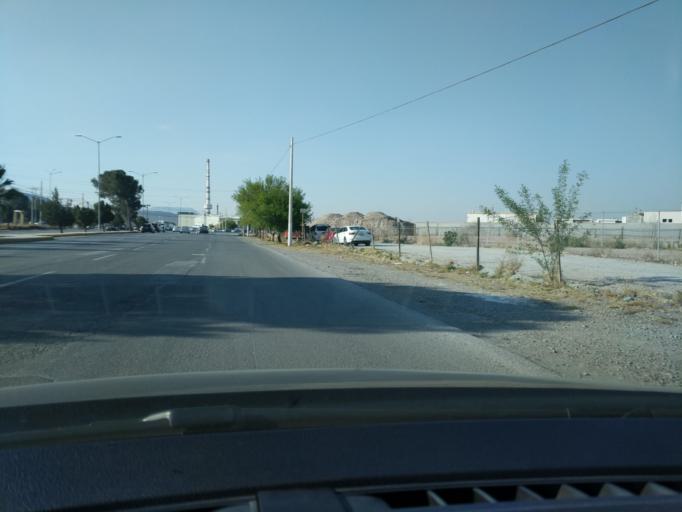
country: MX
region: Coahuila
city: Saltillo
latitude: 25.4771
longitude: -100.9834
